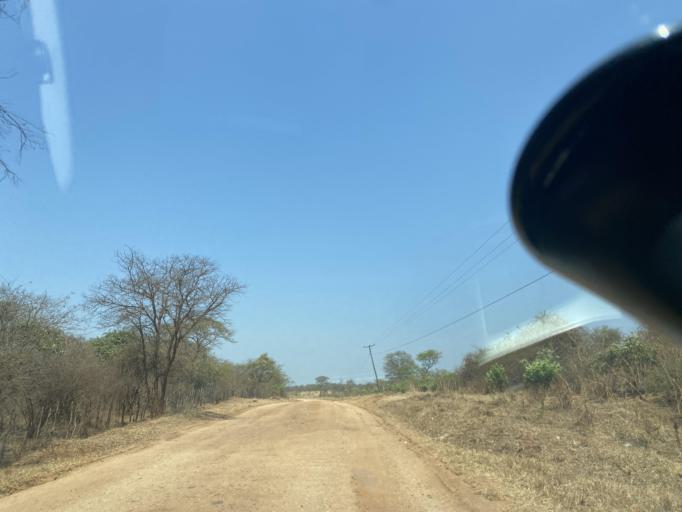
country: ZM
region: Lusaka
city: Lusaka
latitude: -15.5393
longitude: 28.0796
